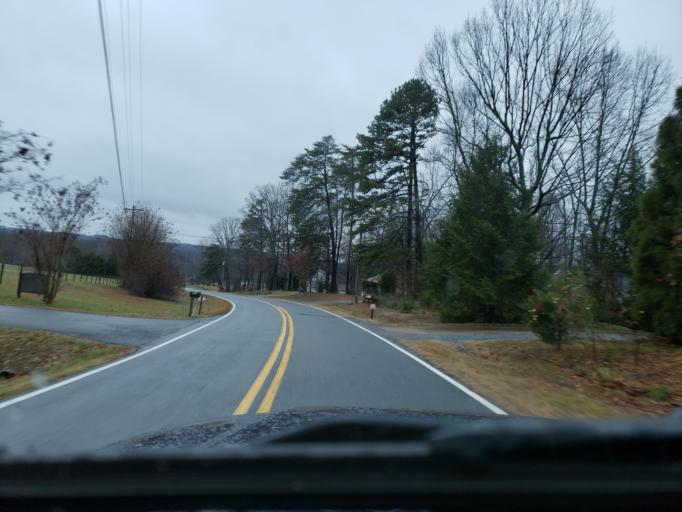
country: US
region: North Carolina
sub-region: Cleveland County
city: White Plains
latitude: 35.1757
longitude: -81.3635
